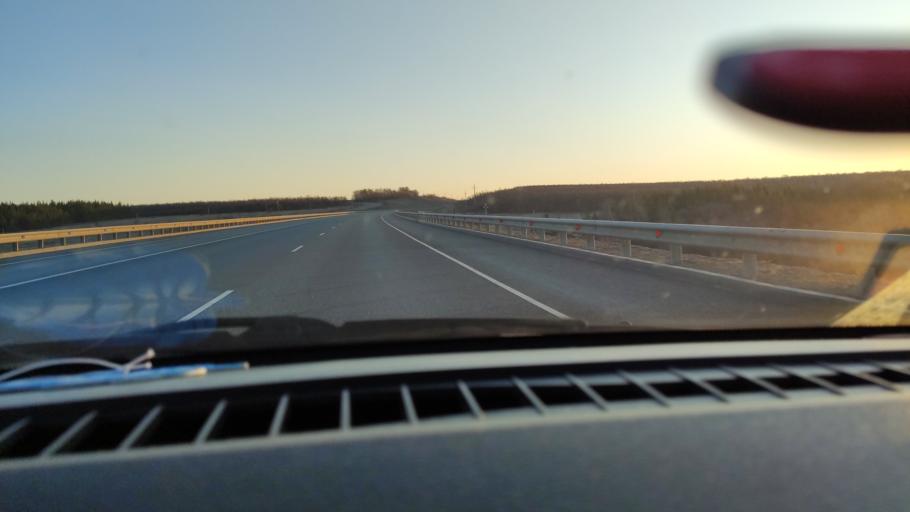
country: RU
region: Saratov
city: Yelshanka
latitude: 51.8792
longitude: 46.5091
